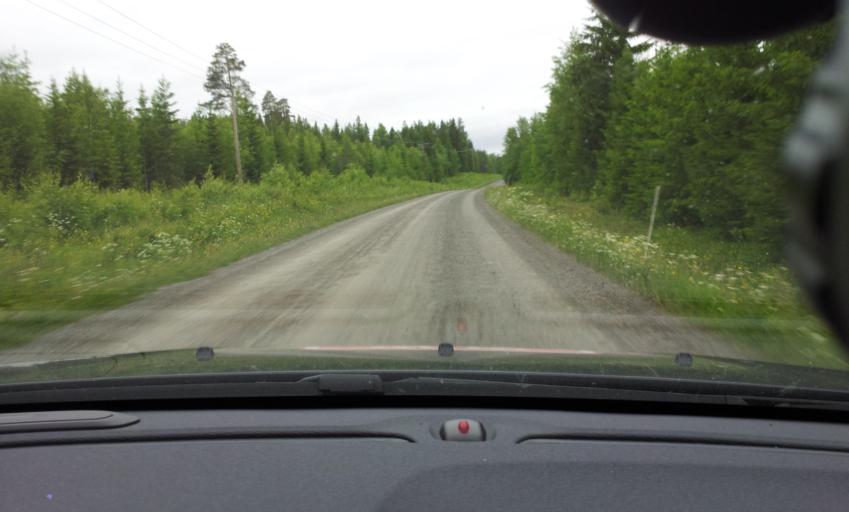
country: SE
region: Jaemtland
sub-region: Krokoms Kommun
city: Valla
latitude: 63.2457
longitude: 13.9674
